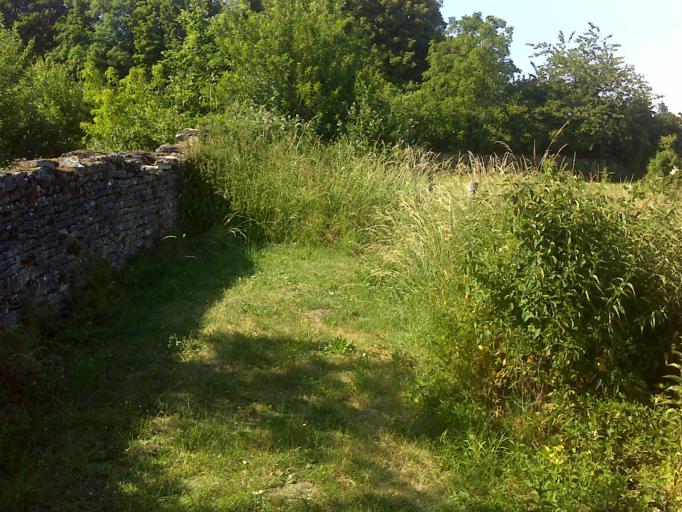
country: FR
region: Bourgogne
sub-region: Departement de la Cote-d'Or
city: Marcilly-sur-Tille
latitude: 47.4908
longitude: 5.2138
